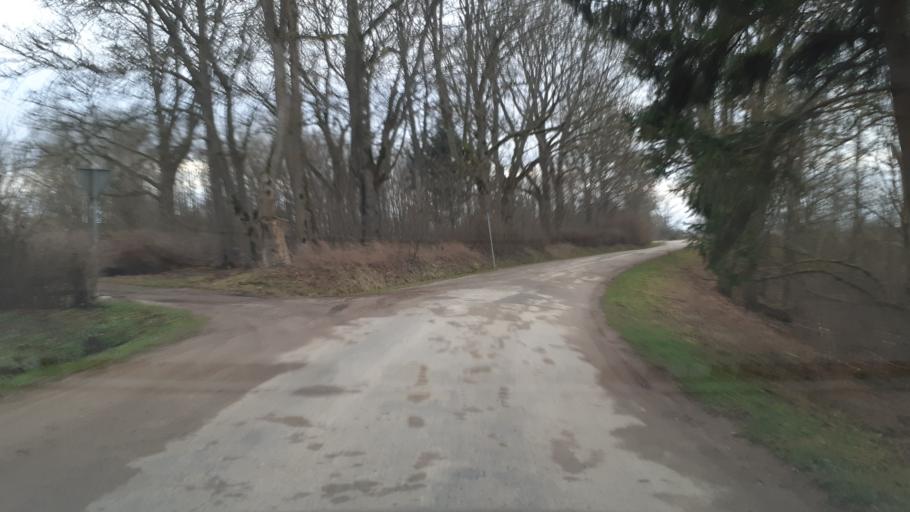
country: LV
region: Aizpute
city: Aizpute
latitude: 56.8021
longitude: 21.6655
